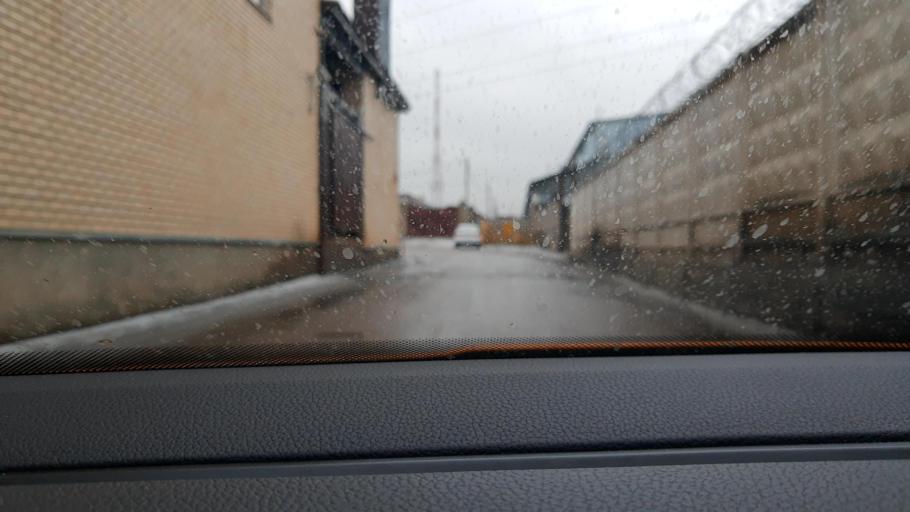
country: RU
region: Moscow
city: Severnyy
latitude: 55.9581
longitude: 37.5439
